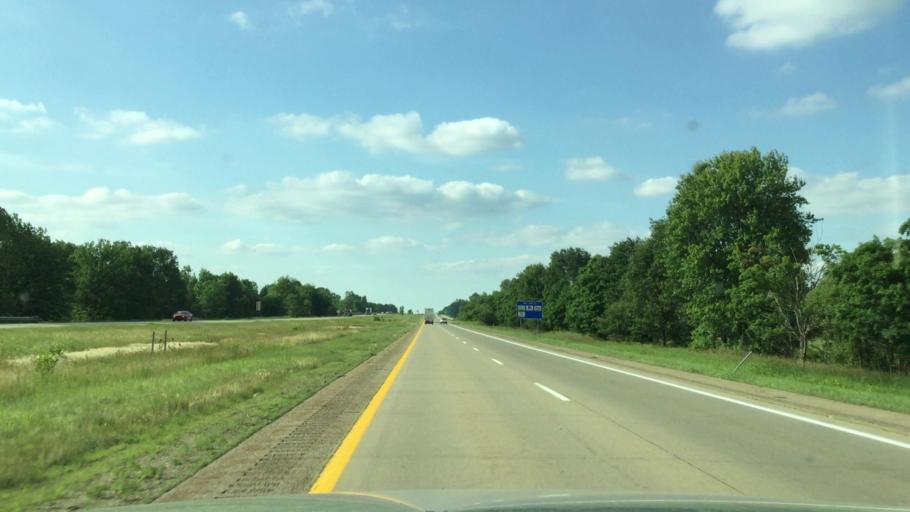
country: US
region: Michigan
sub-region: Branch County
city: Union City
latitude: 42.0921
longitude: -84.9973
